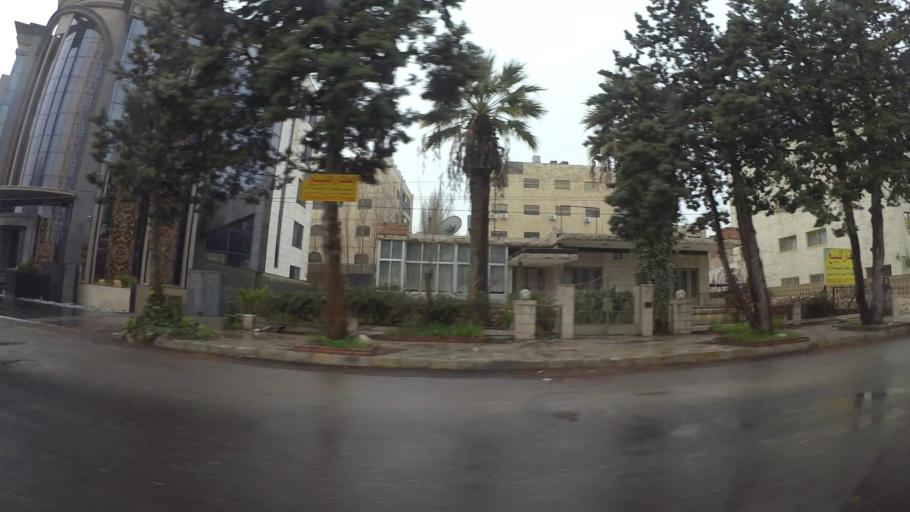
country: JO
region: Amman
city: Wadi as Sir
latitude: 31.9646
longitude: 35.8779
